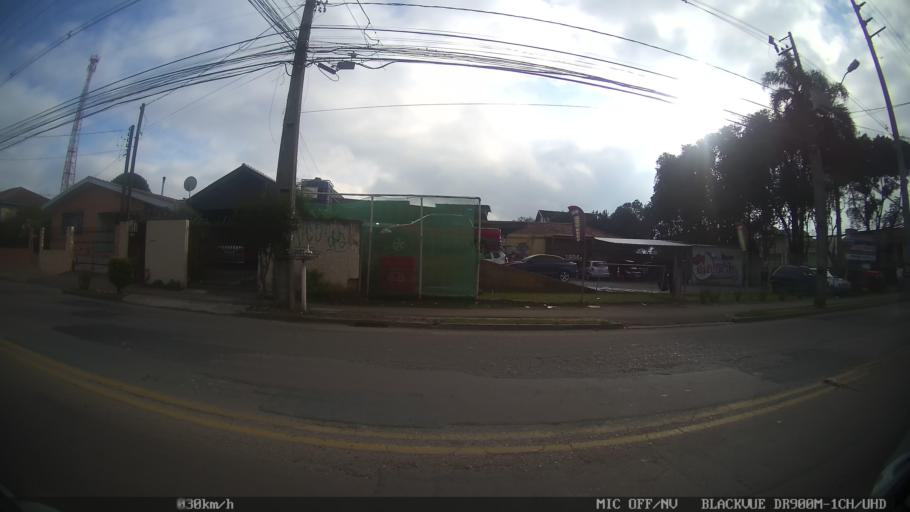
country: BR
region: Parana
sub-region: Almirante Tamandare
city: Almirante Tamandare
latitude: -25.3922
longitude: -49.3371
